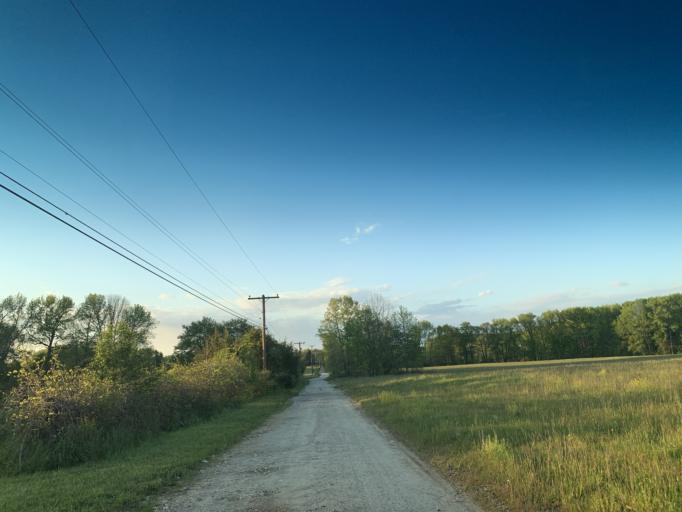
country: US
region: Maryland
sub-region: Harford County
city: Aberdeen
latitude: 39.5075
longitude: -76.1906
